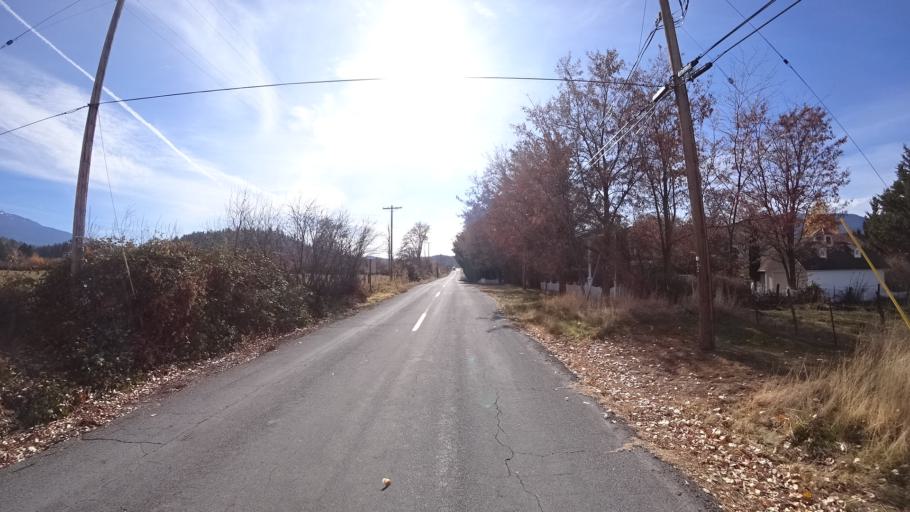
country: US
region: California
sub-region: Siskiyou County
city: Weed
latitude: 41.4565
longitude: -122.4318
